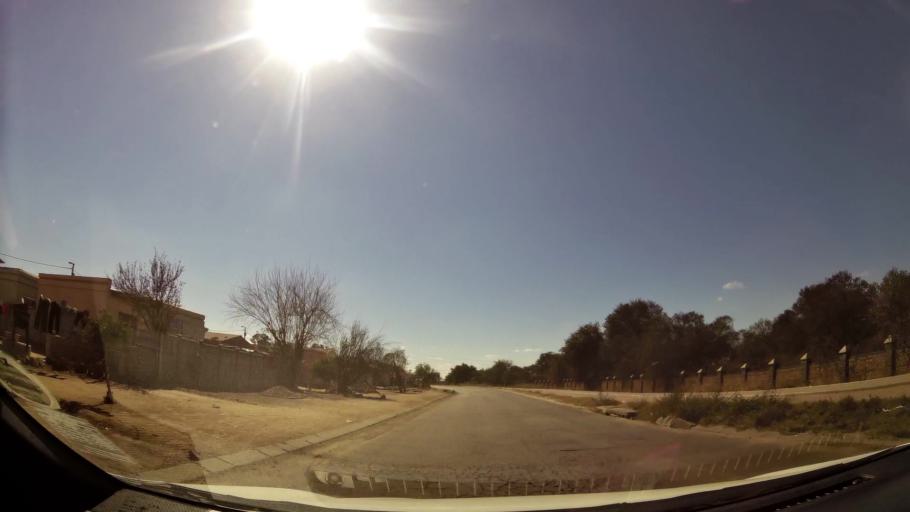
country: ZA
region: Limpopo
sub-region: Capricorn District Municipality
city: Polokwane
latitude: -23.8894
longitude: 29.4243
